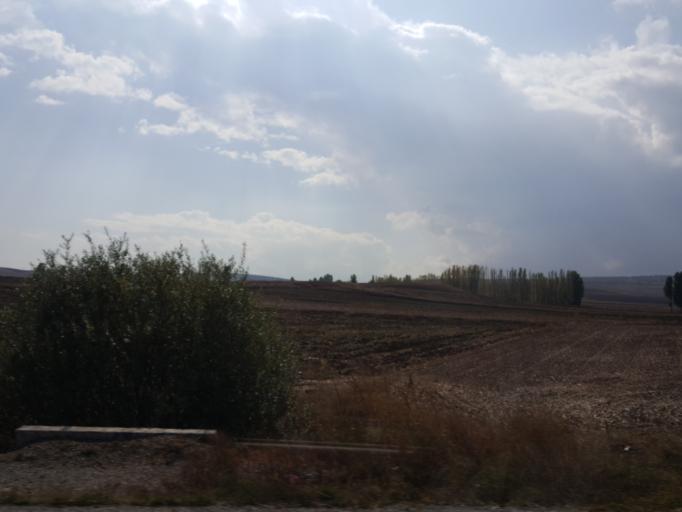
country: TR
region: Corum
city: Alaca
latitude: 40.1387
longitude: 34.8015
